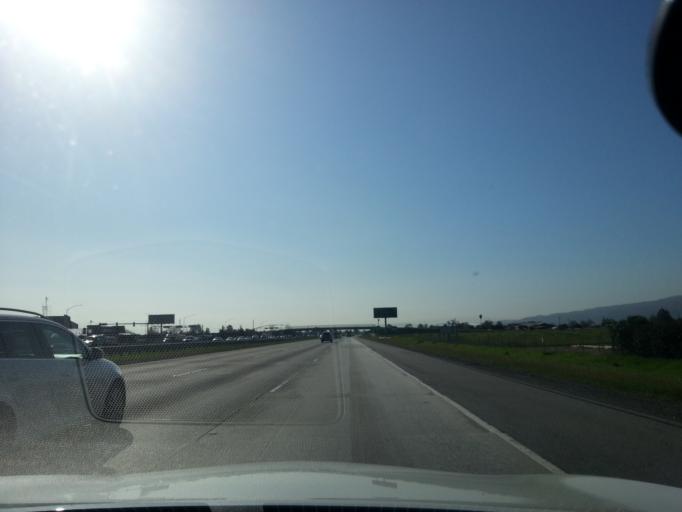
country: US
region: California
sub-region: Santa Clara County
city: San Martin
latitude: 37.0755
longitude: -121.5923
